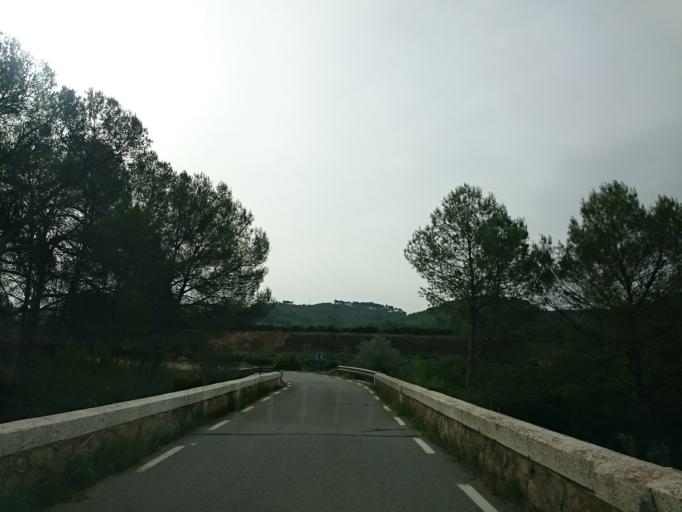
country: ES
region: Catalonia
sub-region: Provincia de Barcelona
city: Olivella
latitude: 41.3114
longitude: 1.7912
